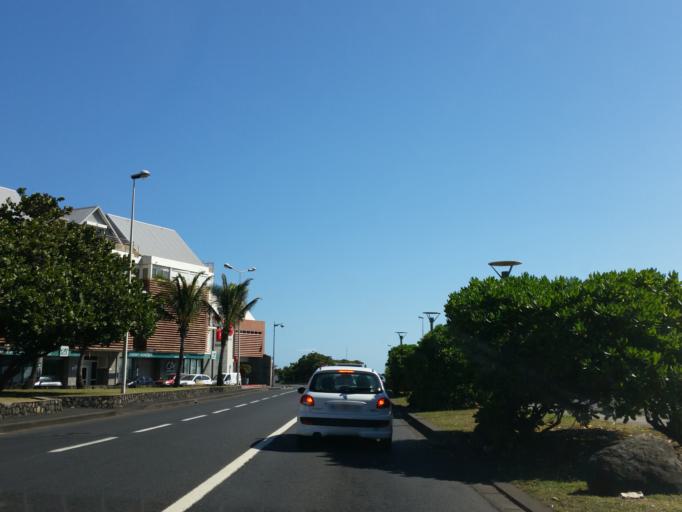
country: RE
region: Reunion
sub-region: Reunion
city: Saint-Denis
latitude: -20.8737
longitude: 55.4526
